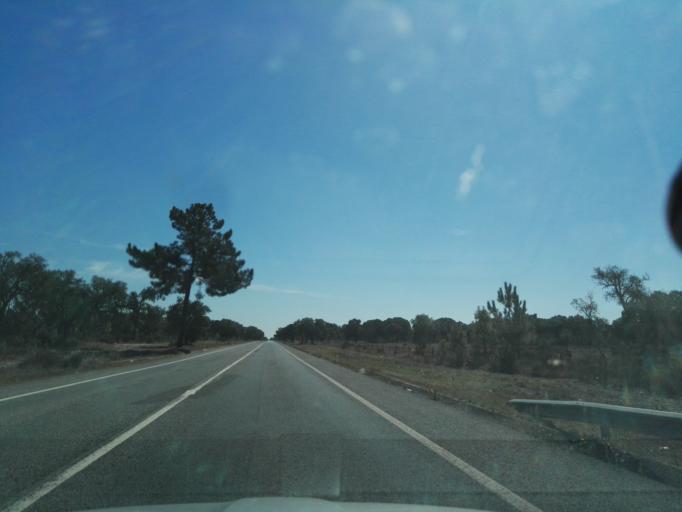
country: PT
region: Santarem
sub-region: Benavente
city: Poceirao
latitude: 38.8886
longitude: -8.8264
